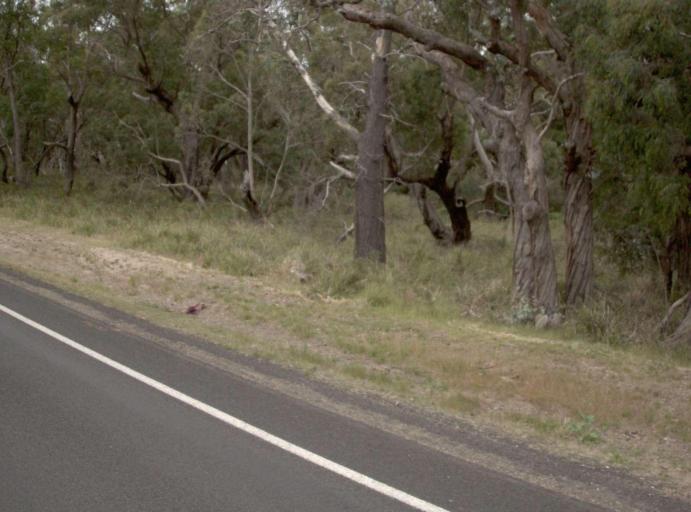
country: AU
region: Victoria
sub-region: Wellington
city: Sale
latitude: -38.2192
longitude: 147.0592
